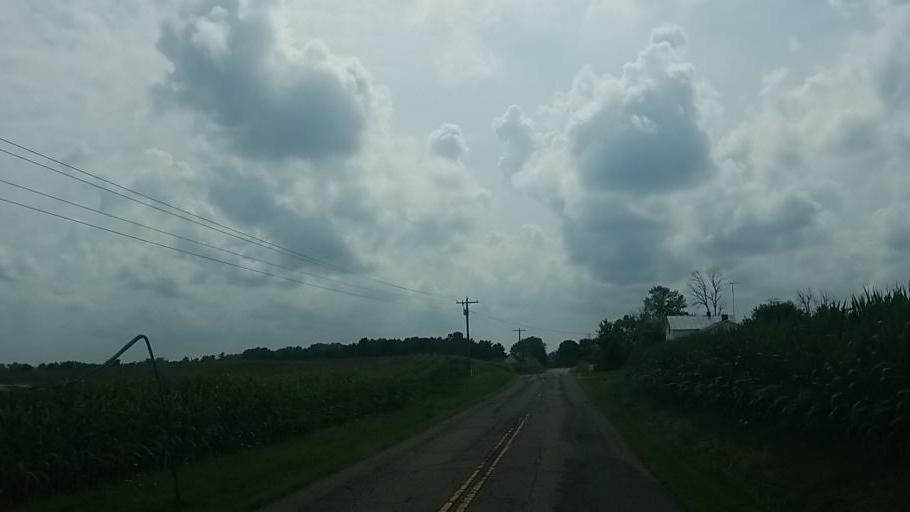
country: US
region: Ohio
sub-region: Knox County
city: Mount Vernon
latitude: 40.3153
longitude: -82.4803
